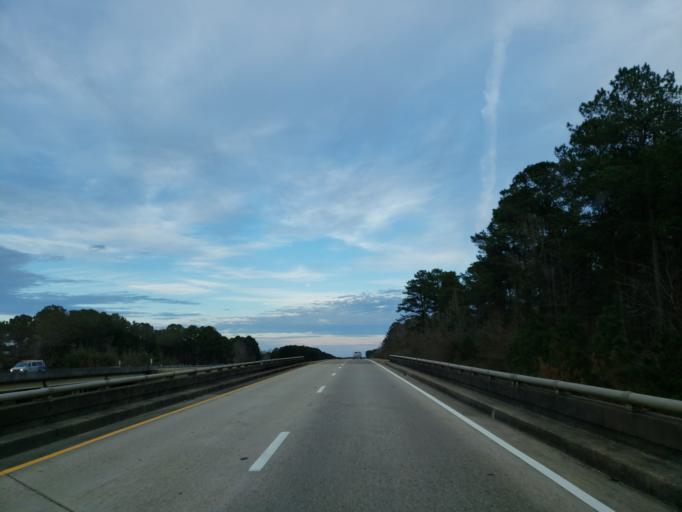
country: US
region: Mississippi
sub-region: Lauderdale County
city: Meridian Station
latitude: 32.4894
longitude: -88.5860
